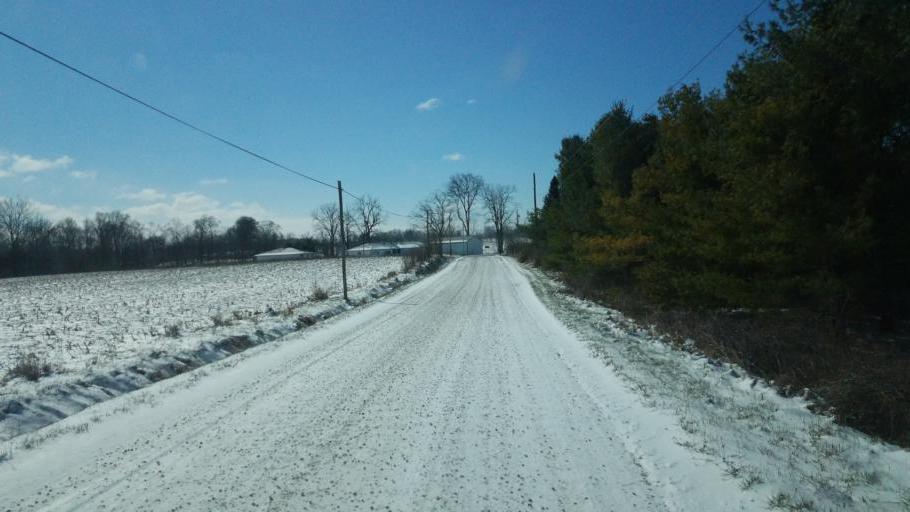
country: US
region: Ohio
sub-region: Morrow County
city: Mount Gilead
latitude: 40.4888
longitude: -82.7192
